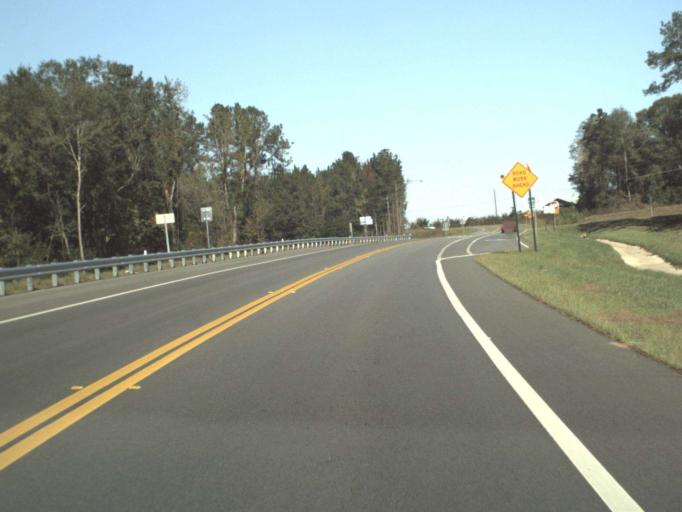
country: US
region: Florida
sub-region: Gadsden County
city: Quincy
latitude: 30.5911
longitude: -84.5538
